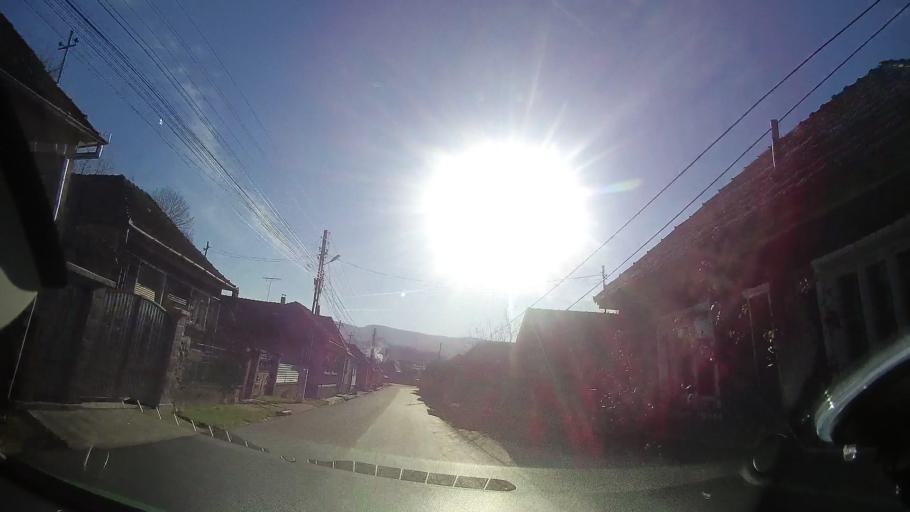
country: RO
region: Bihor
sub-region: Comuna Vadu Crisului
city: Vadu Crisului
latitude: 46.9919
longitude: 22.5220
